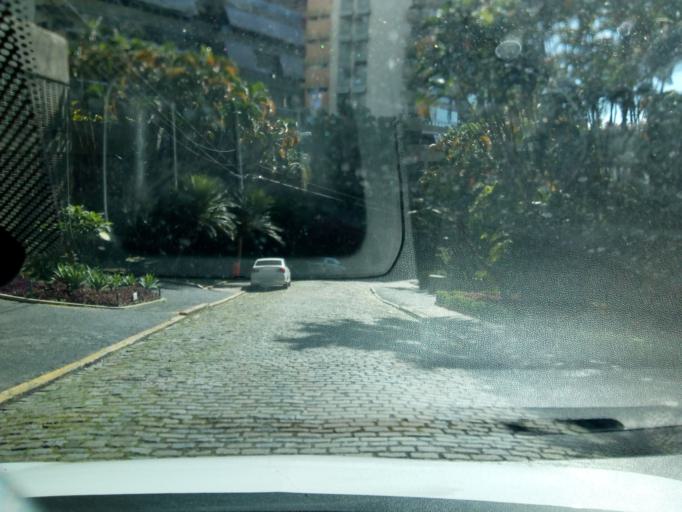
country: BR
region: Rio de Janeiro
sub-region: Rio De Janeiro
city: Rio de Janeiro
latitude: -22.9860
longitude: -43.2355
